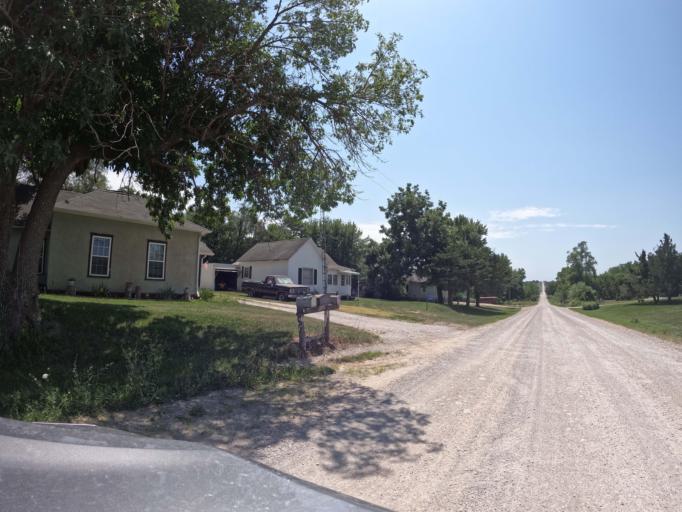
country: US
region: Iowa
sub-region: Appanoose County
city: Centerville
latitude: 40.7860
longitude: -92.9064
